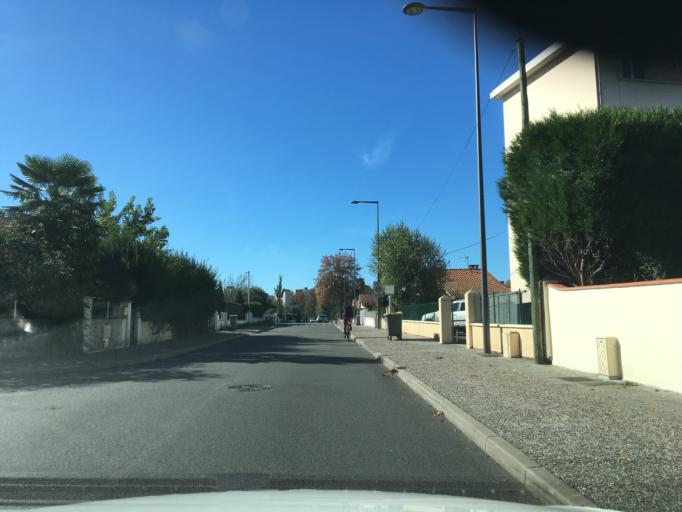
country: FR
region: Aquitaine
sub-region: Departement des Pyrenees-Atlantiques
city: Pau
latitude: 43.3129
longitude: -0.3501
